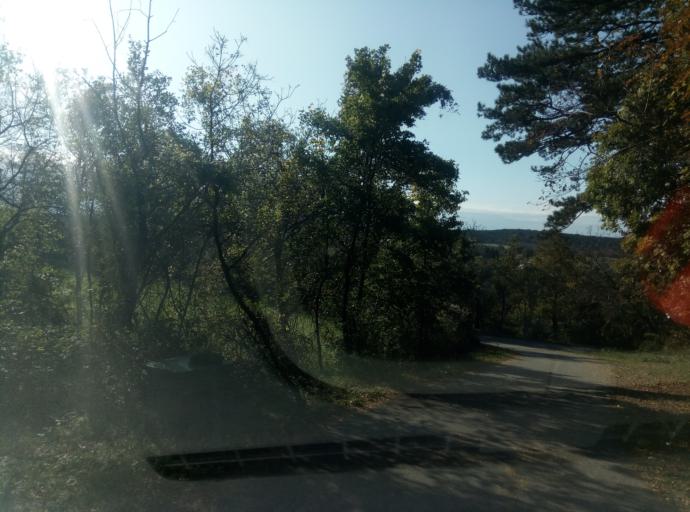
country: SI
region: Ajdovscina
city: Lokavec
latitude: 45.8183
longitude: 13.8532
